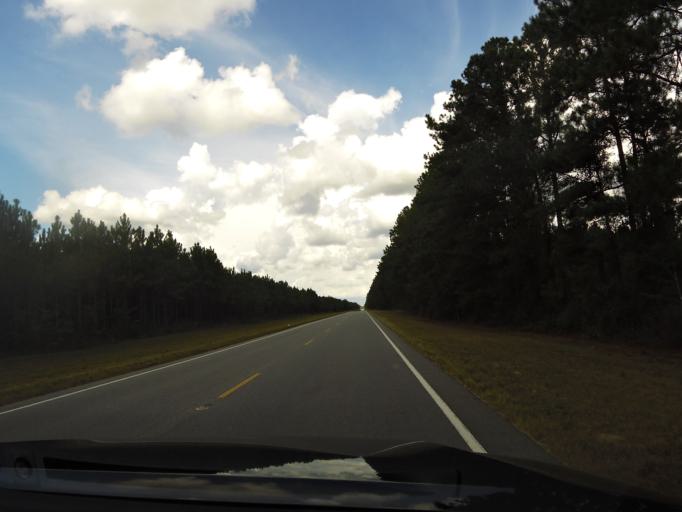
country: US
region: Georgia
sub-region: Charlton County
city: Folkston
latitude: 30.9614
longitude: -82.0239
